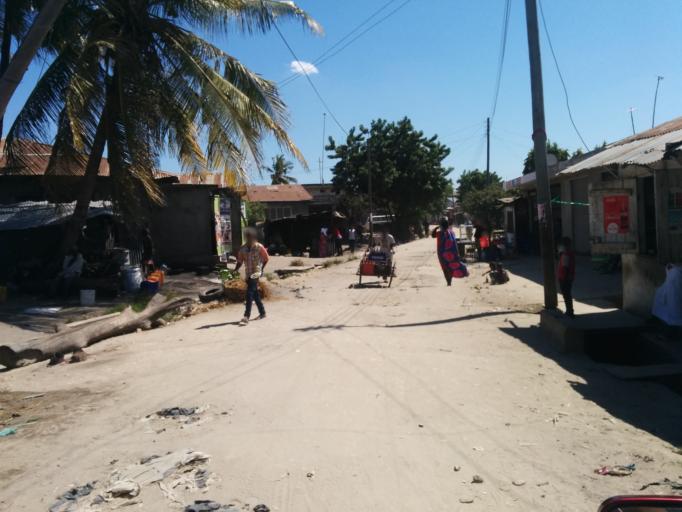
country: TZ
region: Dar es Salaam
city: Magomeni
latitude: -6.7923
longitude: 39.2355
